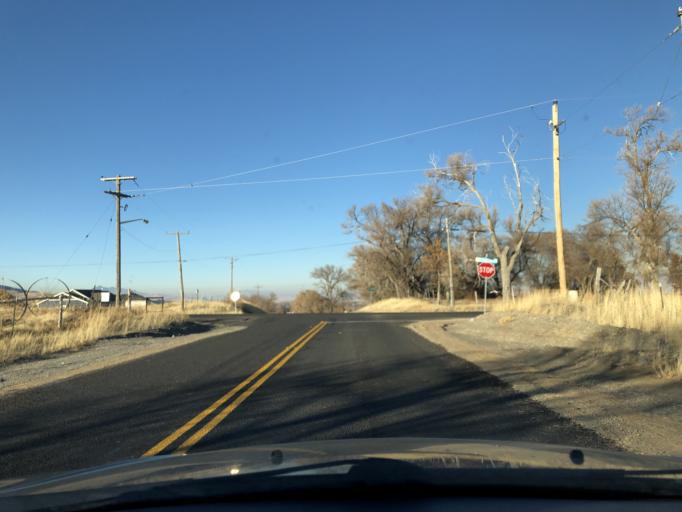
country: US
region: Utah
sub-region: Cache County
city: Wellsville
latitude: 41.6069
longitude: -111.9298
